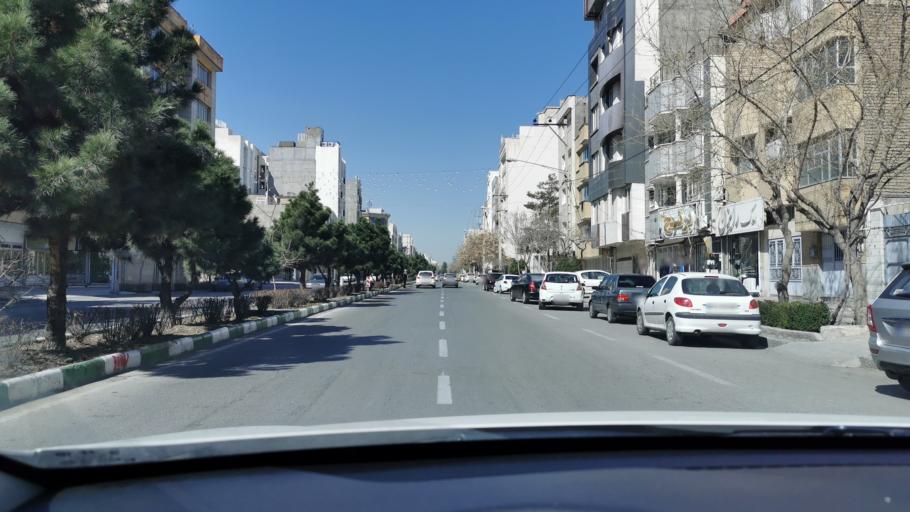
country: IR
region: Razavi Khorasan
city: Mashhad
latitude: 36.3247
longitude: 59.5258
